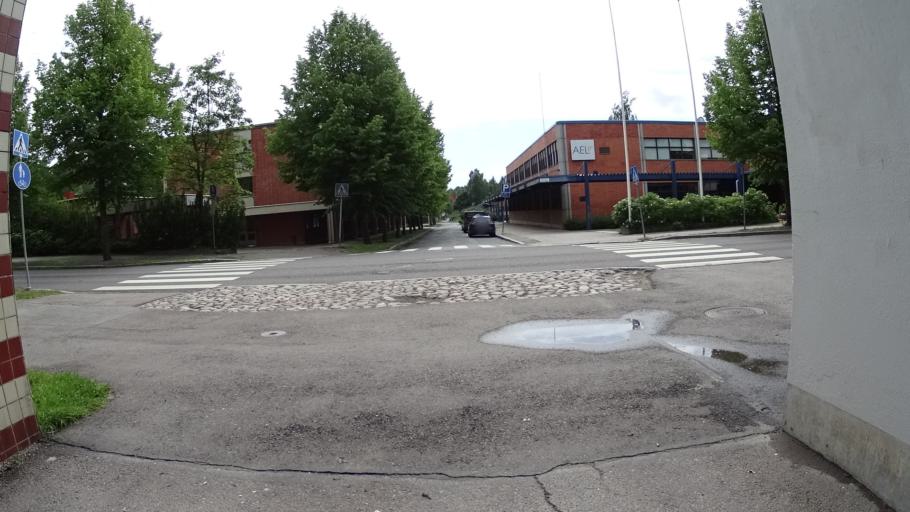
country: FI
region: Uusimaa
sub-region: Helsinki
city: Teekkarikylae
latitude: 60.2500
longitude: 24.8550
